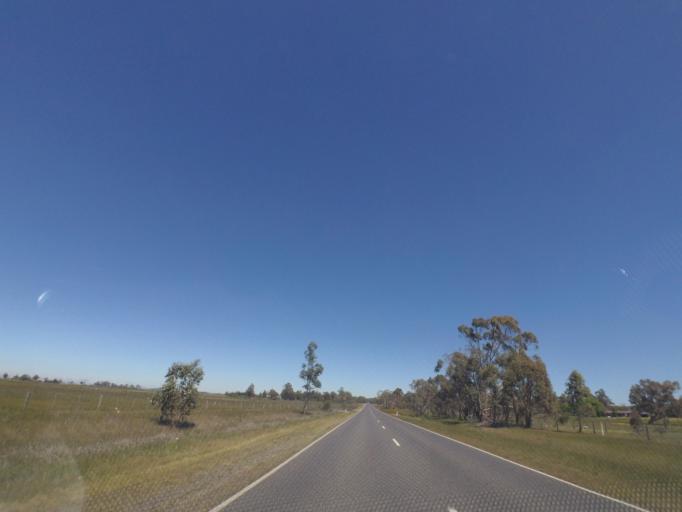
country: AU
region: Victoria
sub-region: Hume
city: Craigieburn
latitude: -37.2912
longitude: 144.8845
